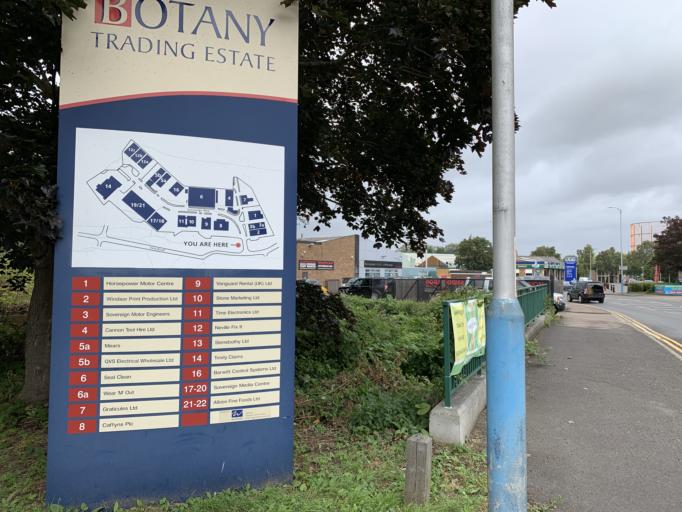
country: GB
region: England
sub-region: Kent
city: Tonbridge
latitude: 51.1907
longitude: 0.2828
